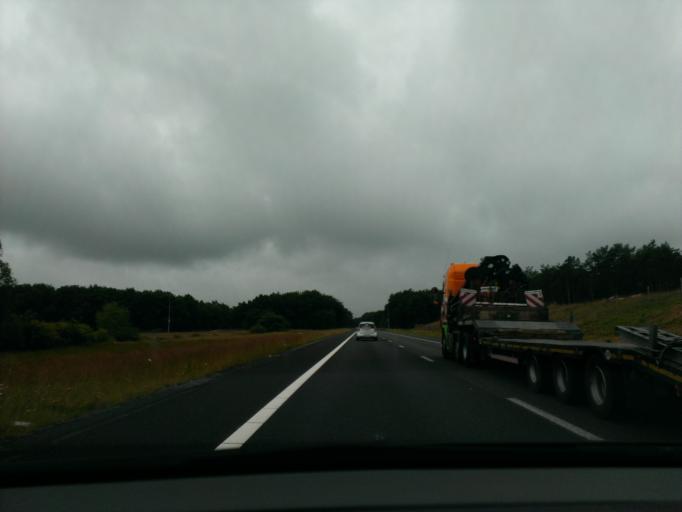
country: NL
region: Drenthe
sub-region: Gemeente Hoogeveen
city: Hoogeveen
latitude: 52.7966
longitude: 6.4528
